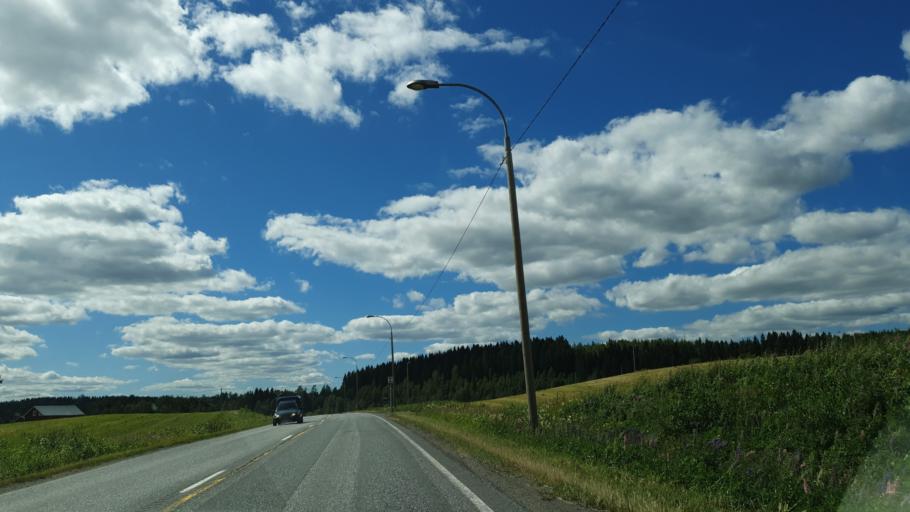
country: FI
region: Northern Savo
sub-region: Kuopio
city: Nilsiae
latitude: 63.1341
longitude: 28.0159
